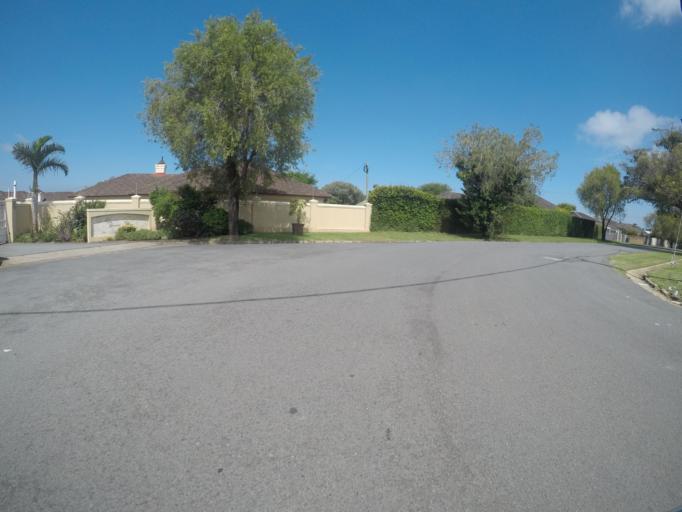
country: ZA
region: Eastern Cape
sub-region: Buffalo City Metropolitan Municipality
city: East London
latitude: -32.9776
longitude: 27.9063
